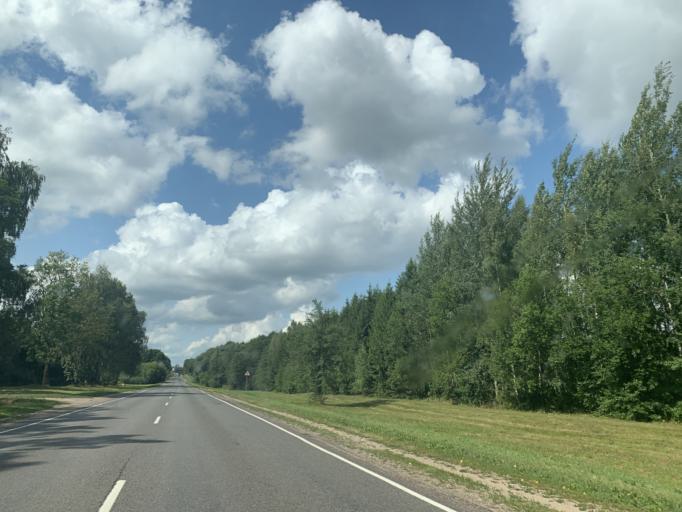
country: BY
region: Minsk
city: Enyerhyetykaw
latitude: 53.5765
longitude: 27.0588
